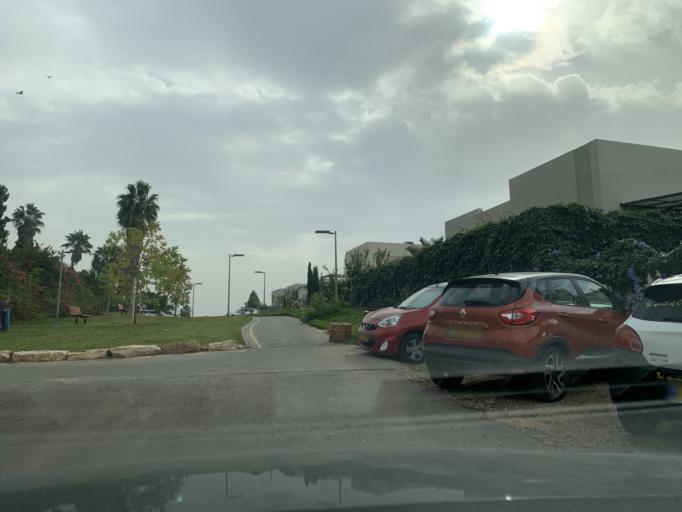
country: IL
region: Central District
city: Tirah
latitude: 32.2170
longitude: 34.9347
